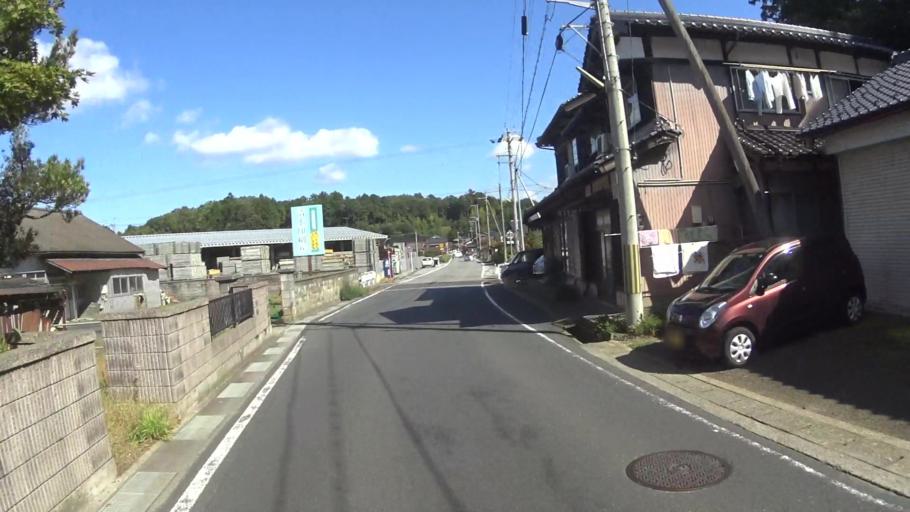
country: JP
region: Kyoto
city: Miyazu
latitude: 35.6306
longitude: 135.0712
